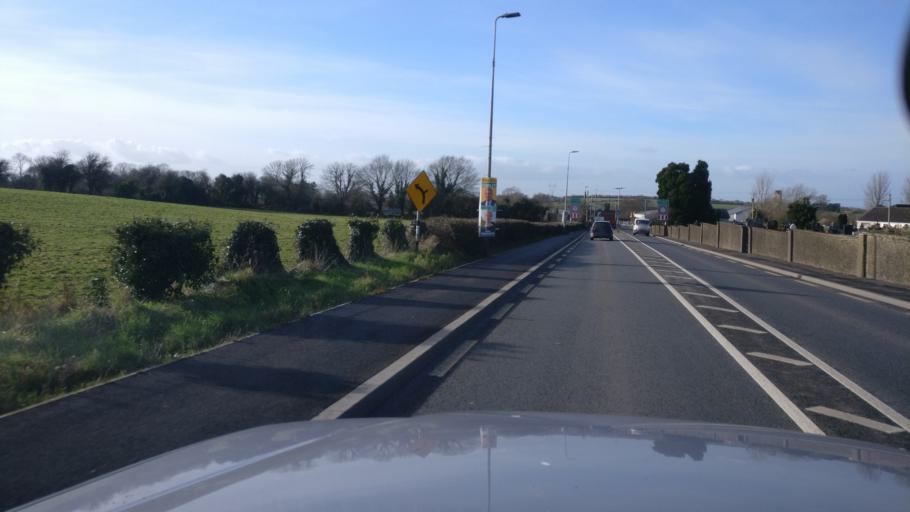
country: IE
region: Leinster
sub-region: Uibh Fhaili
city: Tullamore
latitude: 53.2130
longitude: -7.4444
